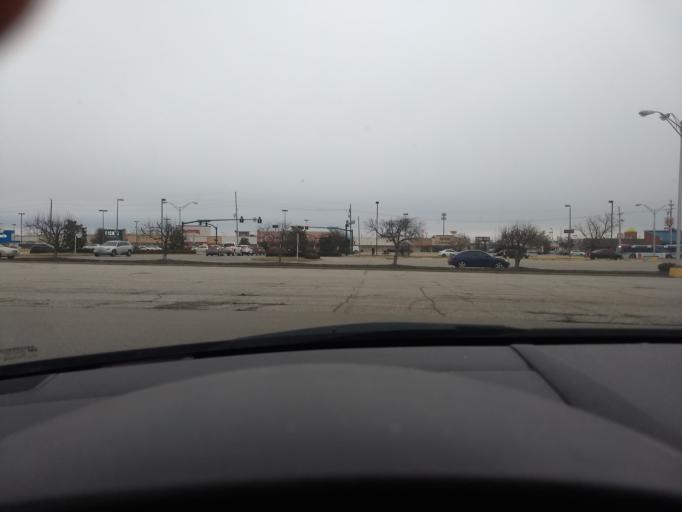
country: US
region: Indiana
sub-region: Clark County
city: Clarksville
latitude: 38.3155
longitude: -85.7623
